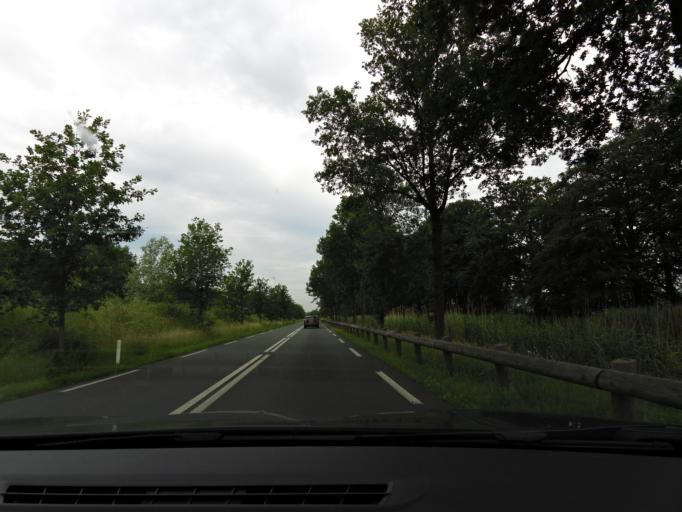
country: NL
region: Gelderland
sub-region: Gemeente Rheden
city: Dieren
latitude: 52.0629
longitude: 6.1003
